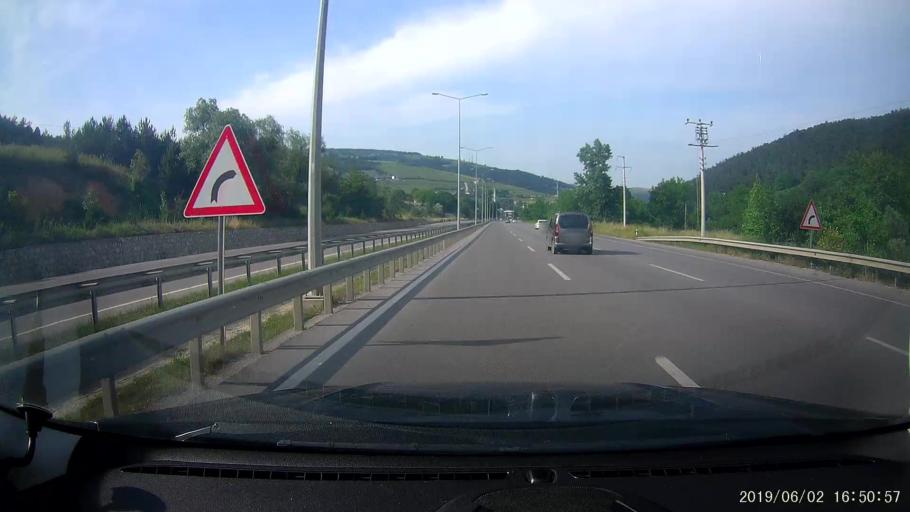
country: TR
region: Samsun
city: Taflan
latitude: 41.2655
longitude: 36.1768
